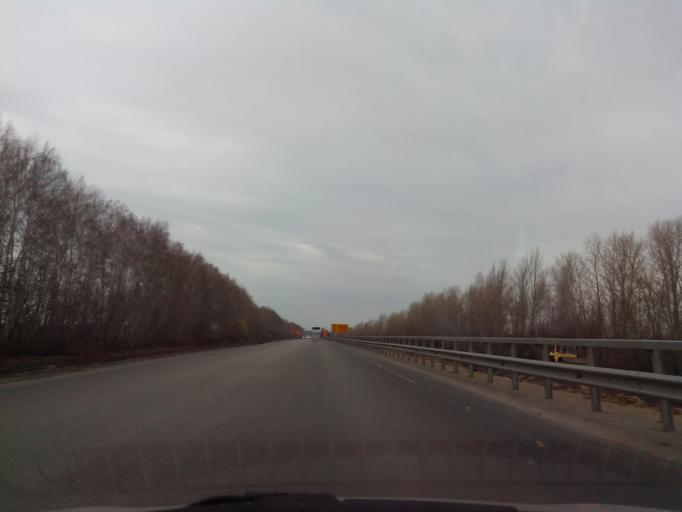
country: RU
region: Tambov
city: Selezni
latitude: 52.8054
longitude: 40.9701
